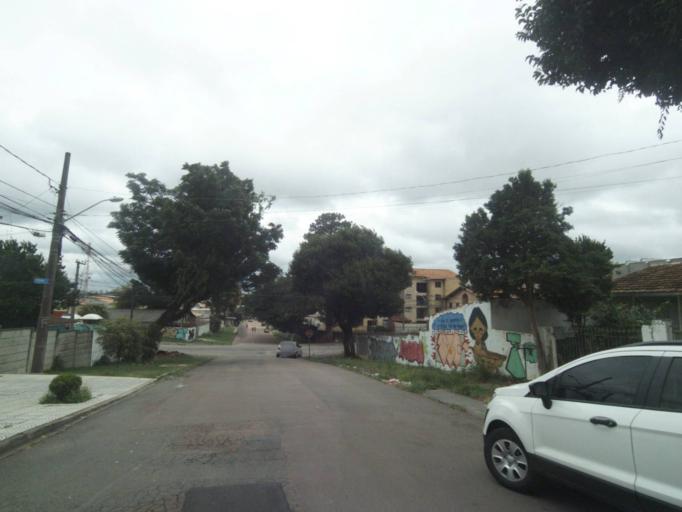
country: BR
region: Parana
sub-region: Curitiba
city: Curitiba
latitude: -25.4930
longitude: -49.3056
